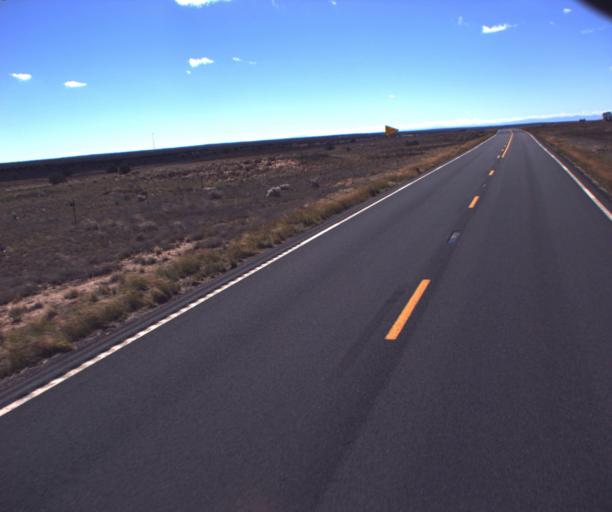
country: US
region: Arizona
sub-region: Apache County
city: Houck
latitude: 34.9350
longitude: -109.2364
